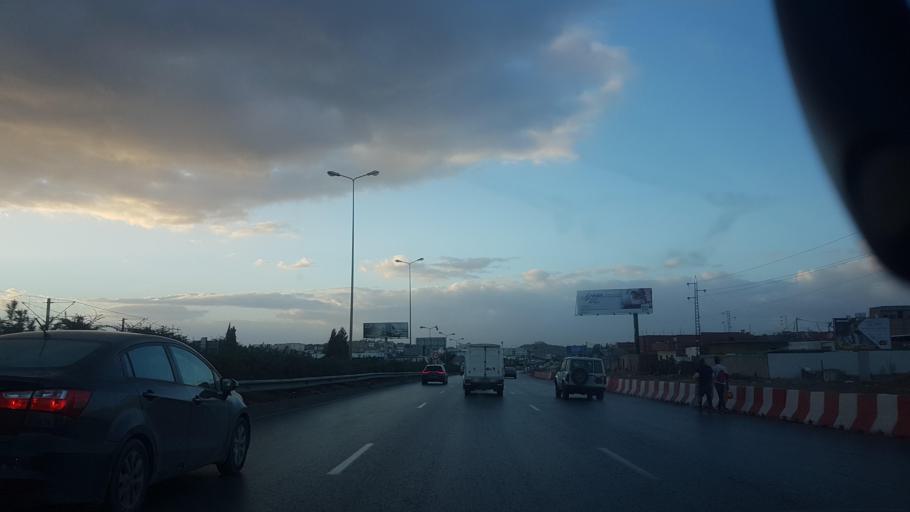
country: TN
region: Bin 'Arus
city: Ben Arous
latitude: 36.7534
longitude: 10.2034
